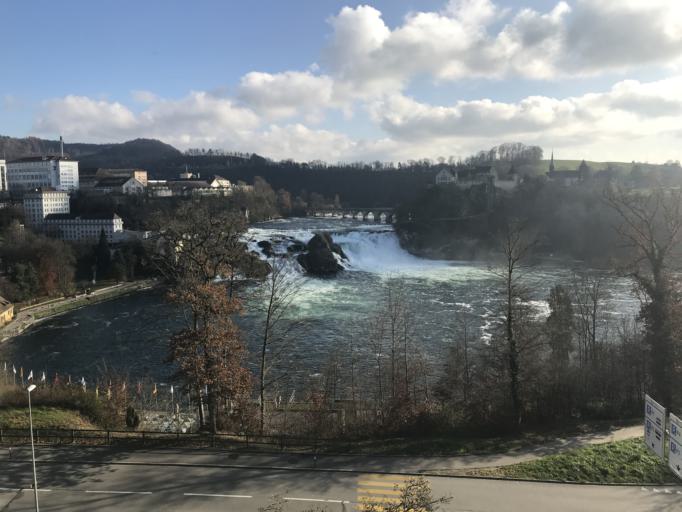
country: CH
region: Schaffhausen
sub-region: Bezirk Schaffhausen
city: Neuhausen
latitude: 47.6801
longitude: 8.6109
